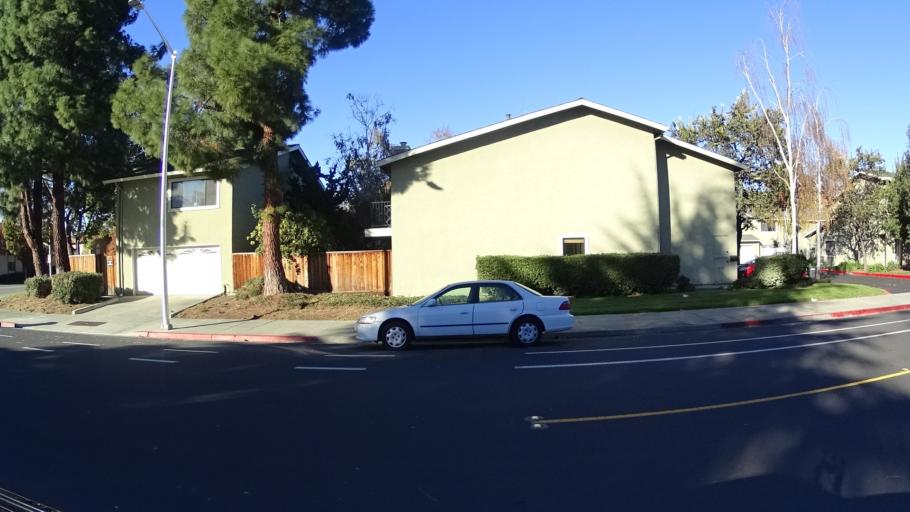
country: US
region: California
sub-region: Santa Clara County
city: Cupertino
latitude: 37.3487
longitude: -121.9987
